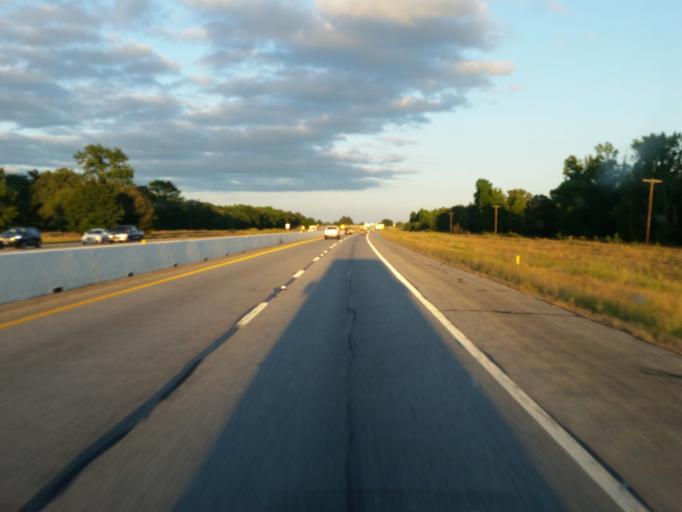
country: US
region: Texas
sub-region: Van Zandt County
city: Van
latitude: 32.5318
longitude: -95.7278
